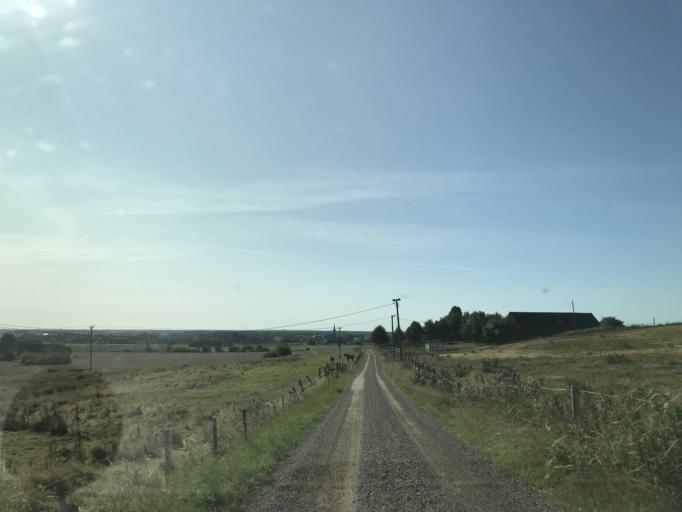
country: SE
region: Skane
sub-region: Landskrona
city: Asmundtorp
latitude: 55.9044
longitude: 12.9497
